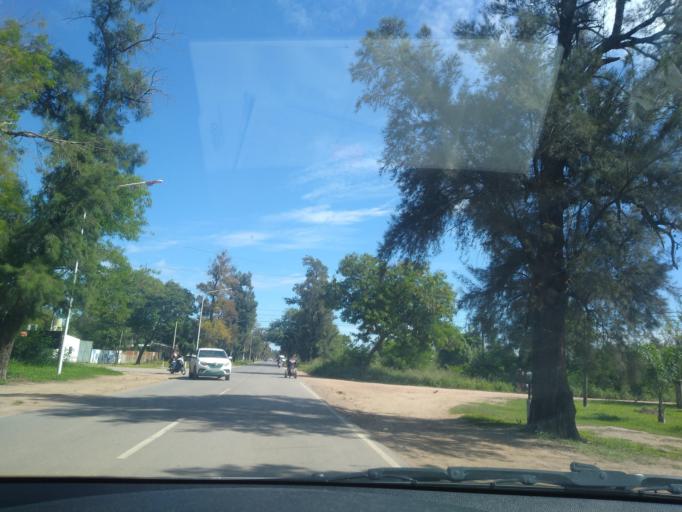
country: AR
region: Chaco
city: Presidencia Roque Saenz Pena
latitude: -26.7715
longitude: -60.4222
